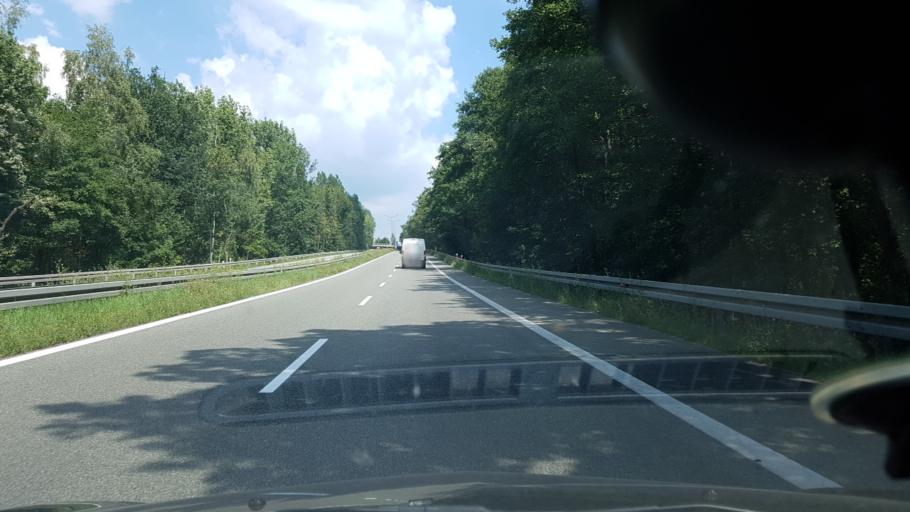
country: PL
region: Silesian Voivodeship
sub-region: Powiat mikolowski
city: Laziska Gorne
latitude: 50.1449
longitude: 18.8461
